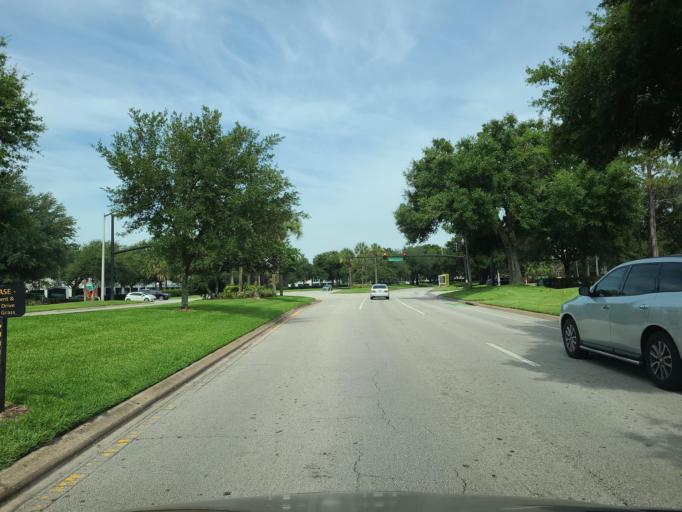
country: US
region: Florida
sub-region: Orange County
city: Orlovista
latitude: 28.5139
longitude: -81.4628
